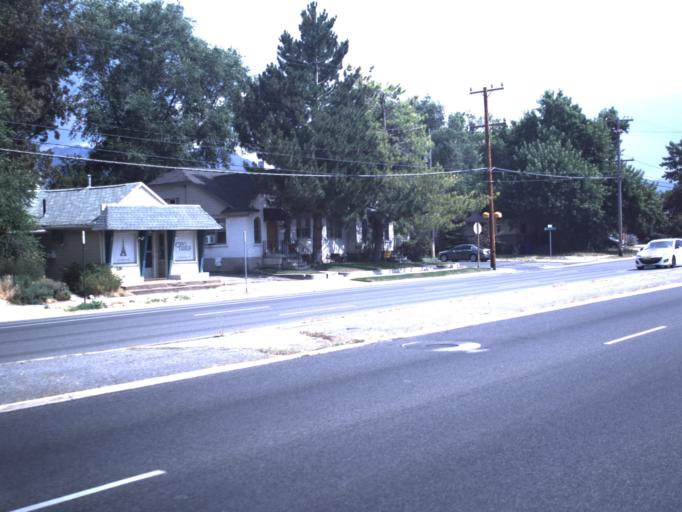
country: US
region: Utah
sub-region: Salt Lake County
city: South Salt Lake
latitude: 40.7324
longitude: -111.8713
